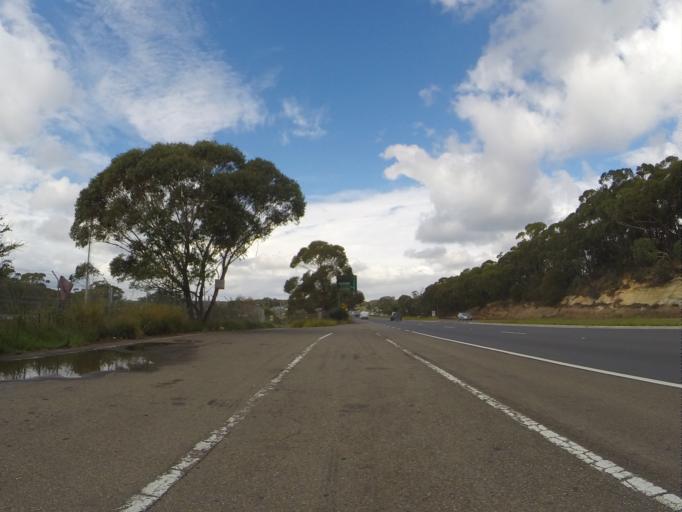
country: AU
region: New South Wales
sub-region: Wollongong
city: Helensburgh
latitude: -34.1293
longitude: 150.9935
